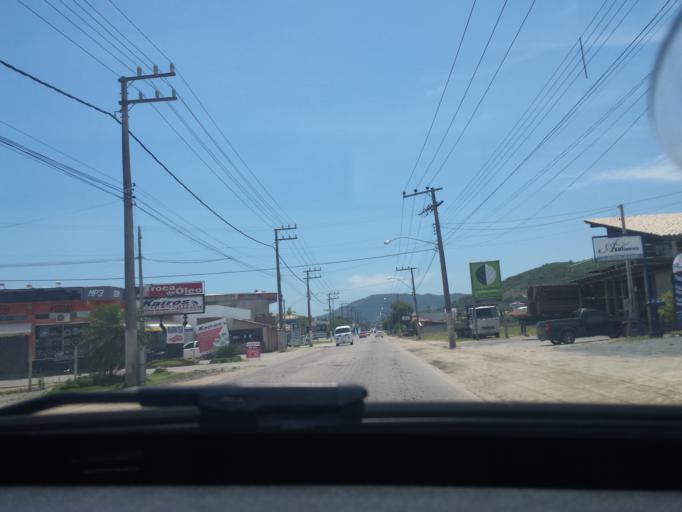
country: BR
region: Santa Catarina
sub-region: Porto Belo
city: Porto Belo
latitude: -27.1596
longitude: -48.5697
